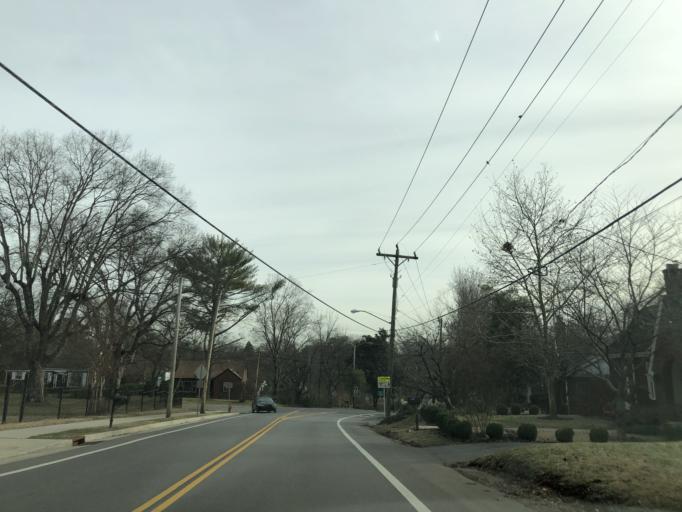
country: US
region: Tennessee
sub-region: Davidson County
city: Nashville
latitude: 36.2094
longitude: -86.7244
